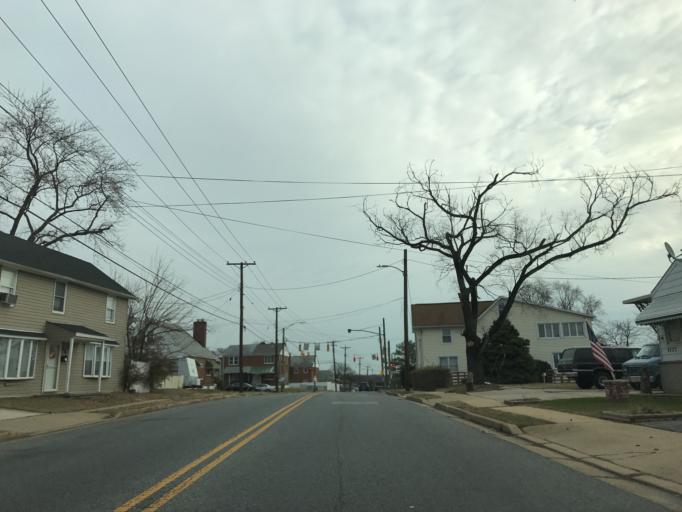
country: US
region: Maryland
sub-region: Baltimore County
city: Overlea
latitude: 39.3418
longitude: -76.5331
